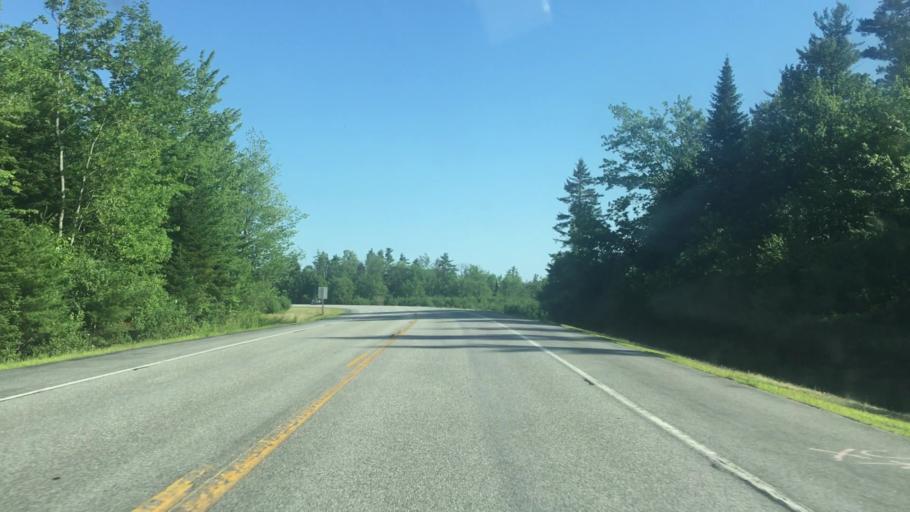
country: US
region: Maine
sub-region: Cumberland County
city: Gorham
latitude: 43.6536
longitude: -70.4483
